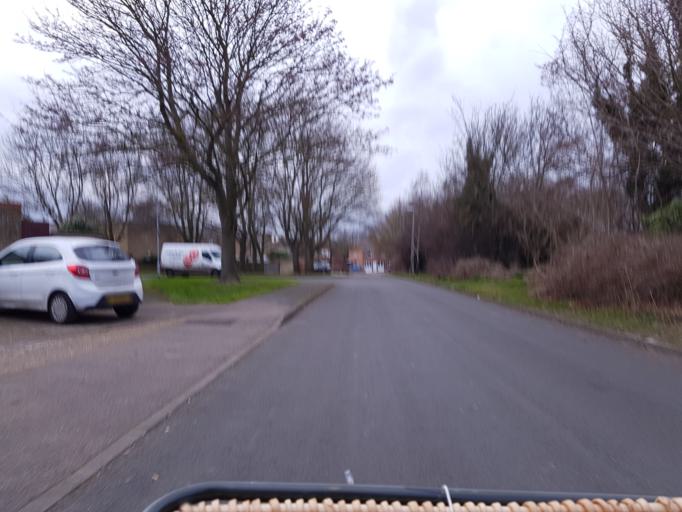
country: GB
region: England
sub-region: Cambridgeshire
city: Fulbourn
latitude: 52.1952
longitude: 0.1801
